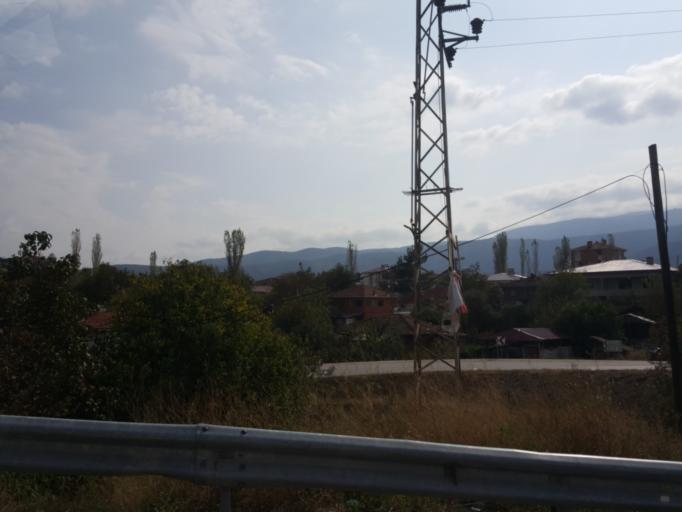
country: TR
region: Corum
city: Hacihamza
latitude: 41.0959
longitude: 34.3536
